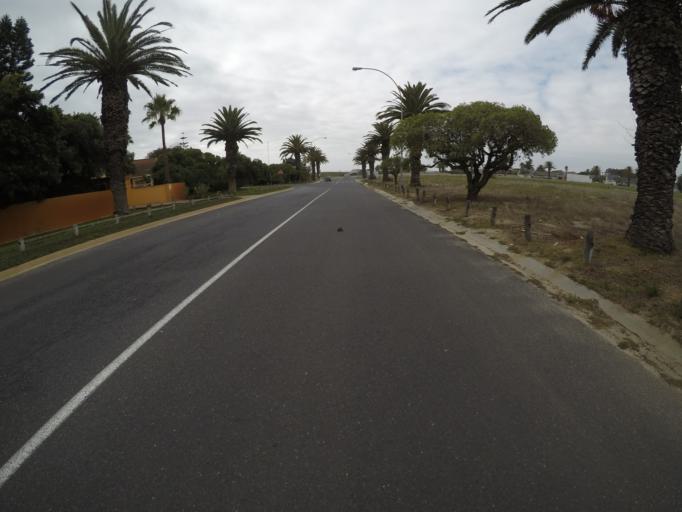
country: ZA
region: Western Cape
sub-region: City of Cape Town
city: Atlantis
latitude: -33.6926
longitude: 18.4426
